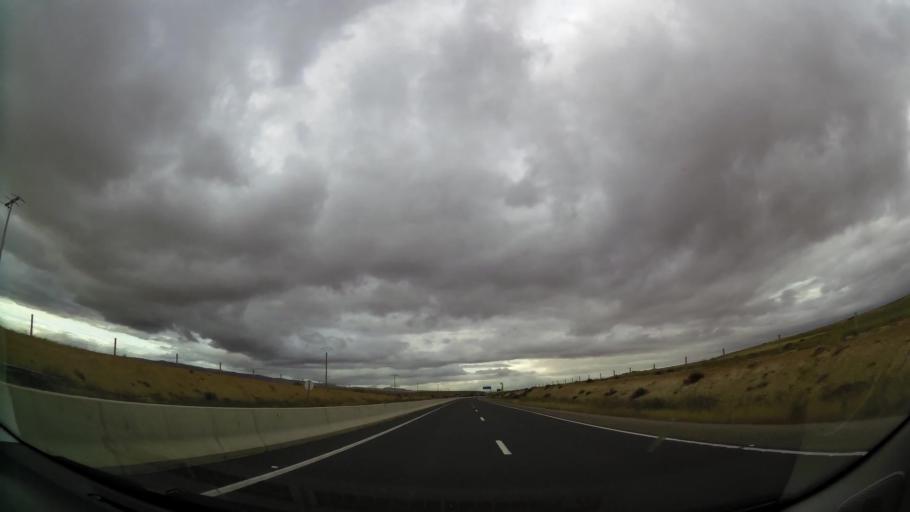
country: MA
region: Taza-Al Hoceima-Taounate
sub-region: Taza
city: Taza
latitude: 34.3077
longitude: -3.7546
